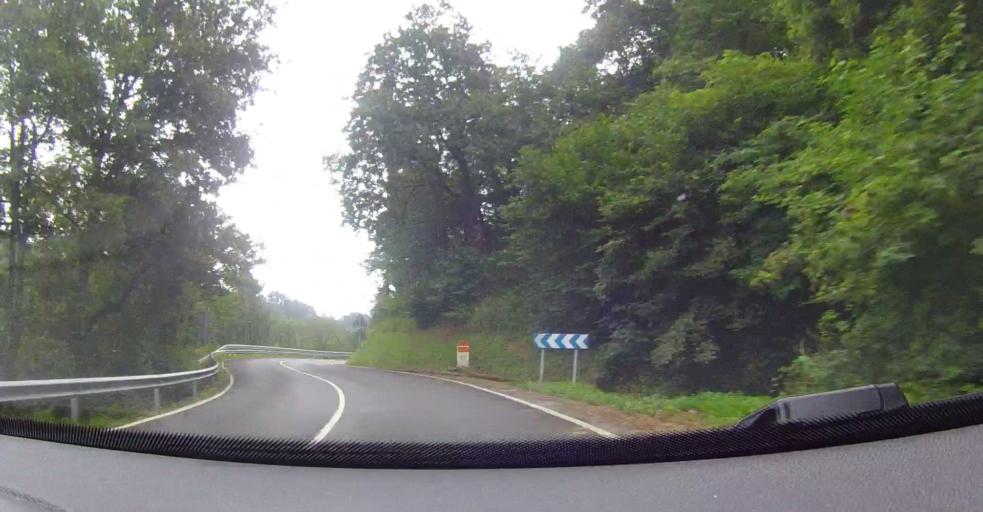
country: ES
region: Basque Country
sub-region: Bizkaia
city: Balmaseda
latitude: 43.2346
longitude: -3.2047
